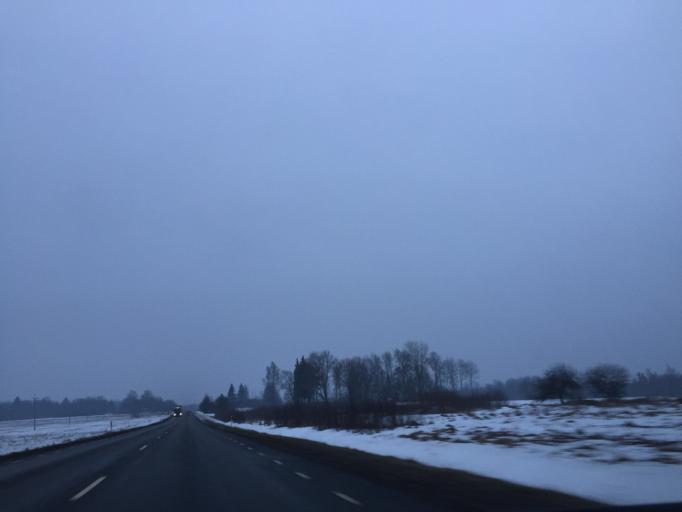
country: EE
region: Laeaene
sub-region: Lihula vald
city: Lihula
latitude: 58.5198
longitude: 24.0792
